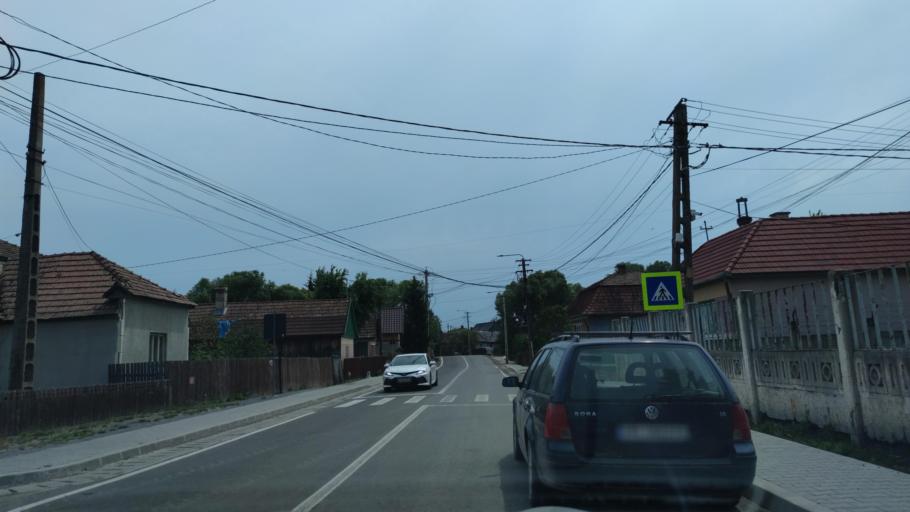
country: RO
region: Harghita
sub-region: Comuna Remetea
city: Remetea
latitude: 46.8122
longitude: 25.4595
